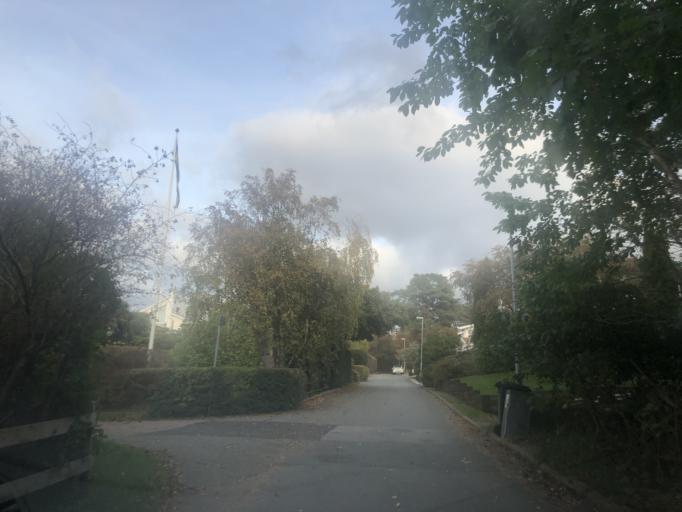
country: SE
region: Vaestra Goetaland
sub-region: Goteborg
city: Billdal
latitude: 57.6277
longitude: 11.9503
